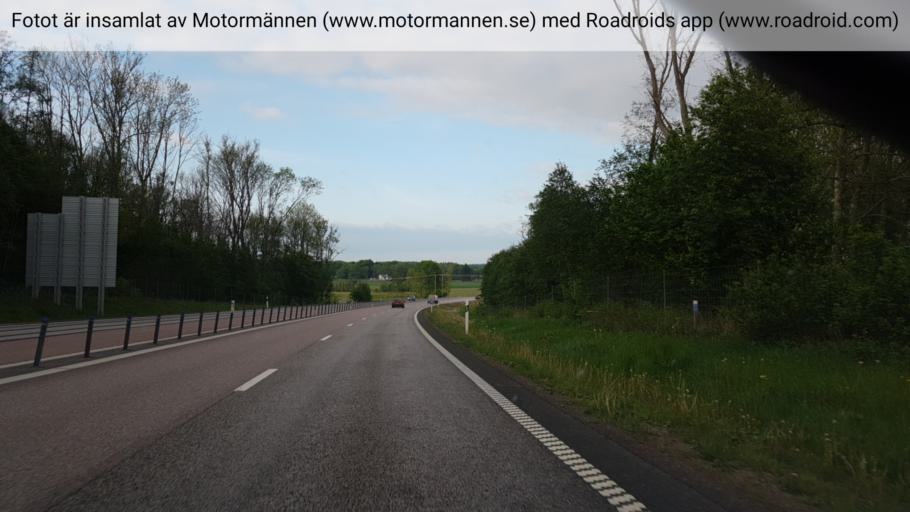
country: SE
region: Vaestra Goetaland
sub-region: Skovde Kommun
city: Skultorp
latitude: 58.3182
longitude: 13.8177
